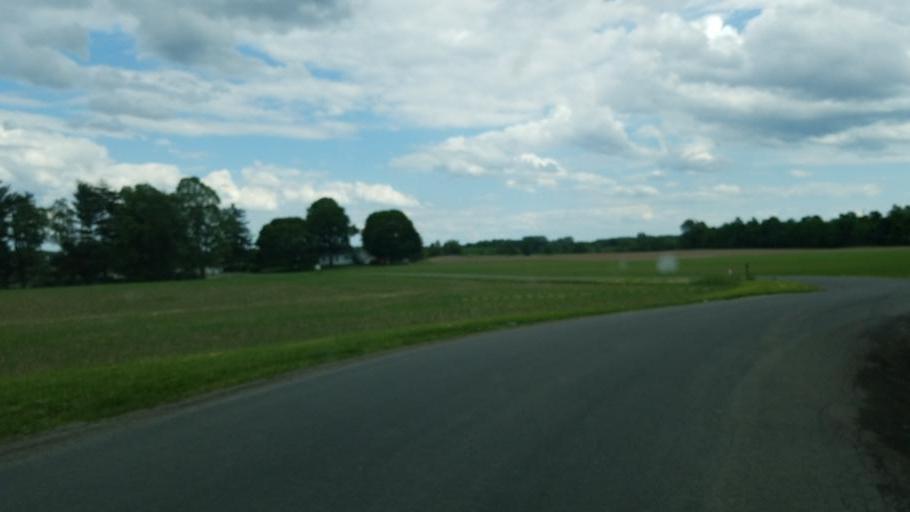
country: US
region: Ohio
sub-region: Richland County
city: Shelby
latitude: 40.9384
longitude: -82.6146
